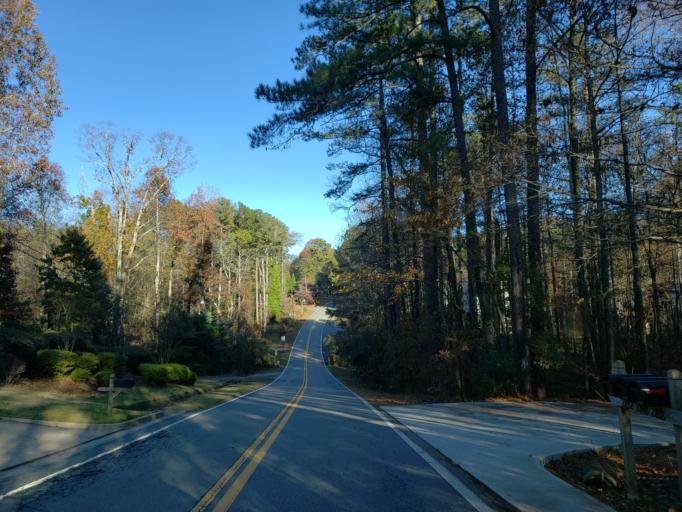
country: US
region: Georgia
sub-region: Cherokee County
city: Woodstock
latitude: 34.0462
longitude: -84.4692
